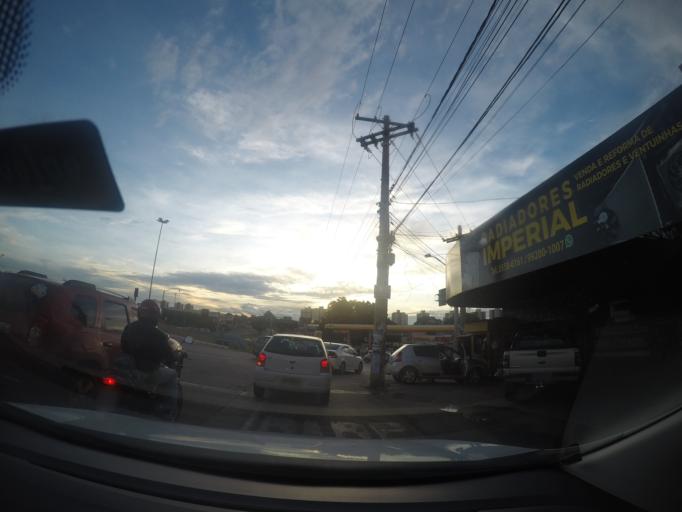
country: BR
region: Goias
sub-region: Goiania
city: Goiania
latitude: -16.6924
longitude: -49.3191
